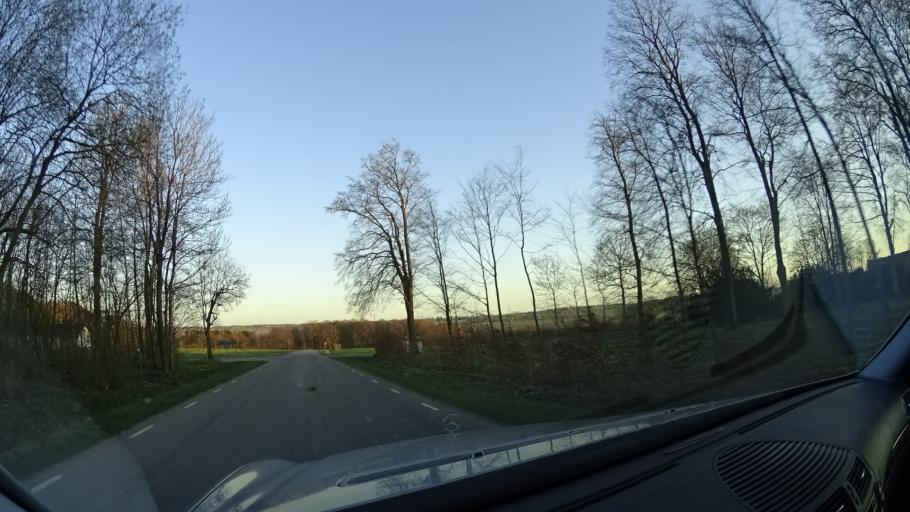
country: SE
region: Skane
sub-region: Hoors Kommun
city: Loberod
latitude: 55.8177
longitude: 13.4459
